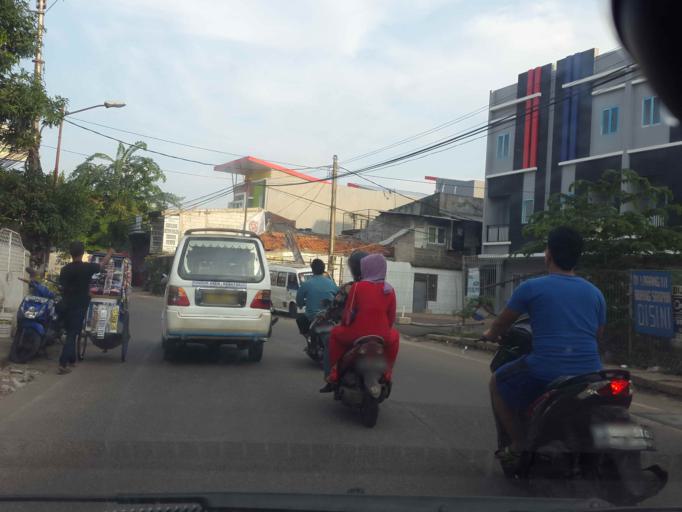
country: ID
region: Banten
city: South Tangerang
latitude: -6.2632
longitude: 106.7265
